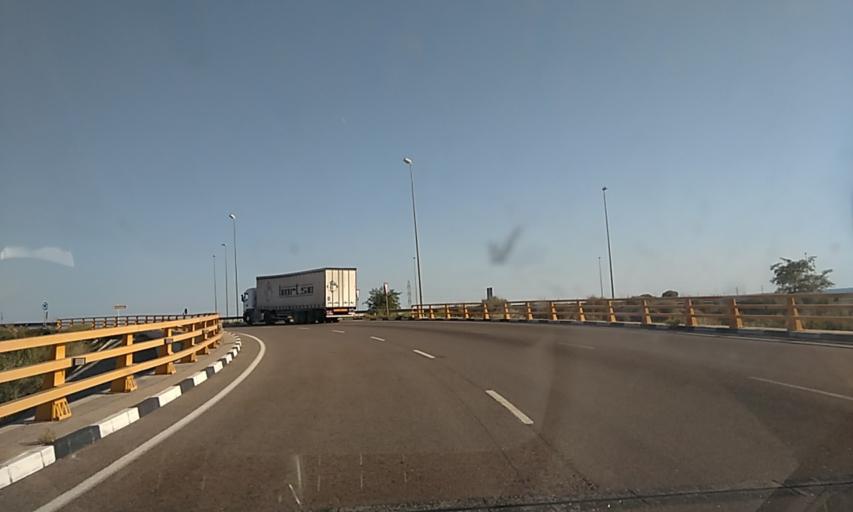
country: ES
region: Valencia
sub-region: Provincia de Castello
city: Torreblanca
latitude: 40.2276
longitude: 0.2125
